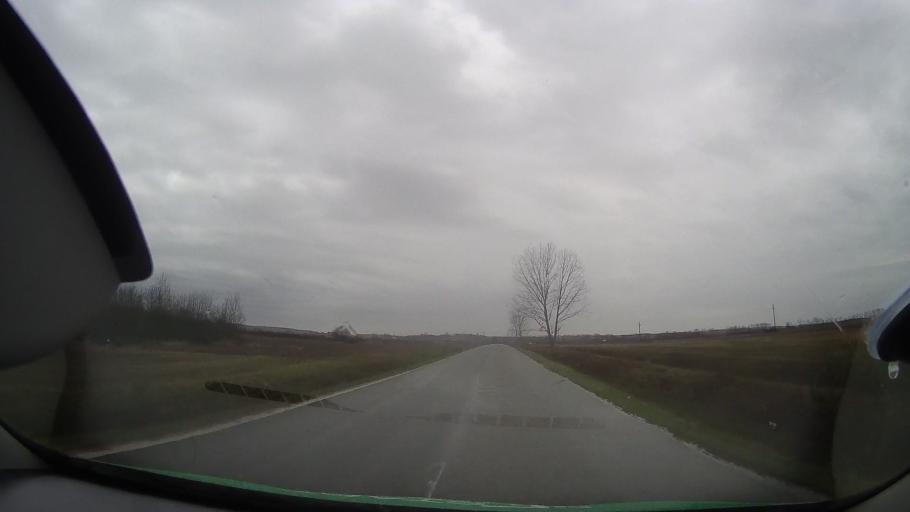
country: RO
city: Capalna
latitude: 46.7126
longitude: 22.0638
